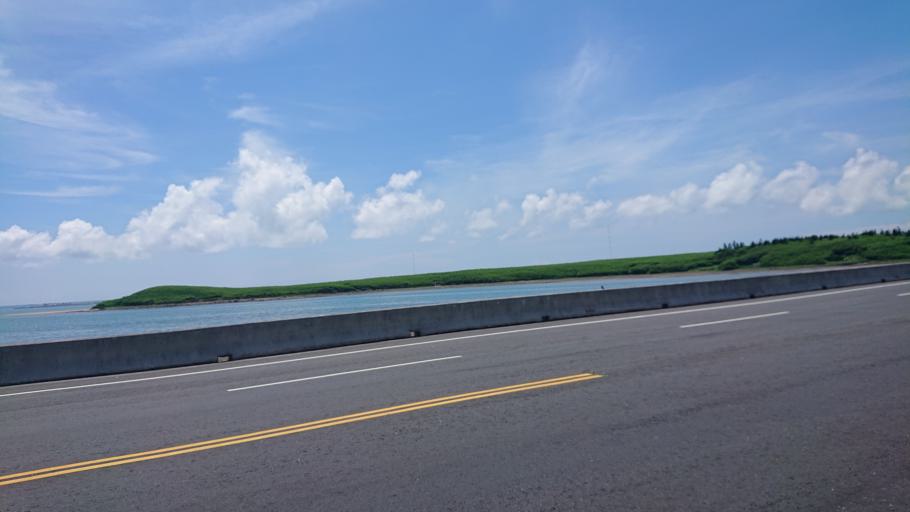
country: TW
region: Taiwan
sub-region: Penghu
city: Ma-kung
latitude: 23.6207
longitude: 119.6055
